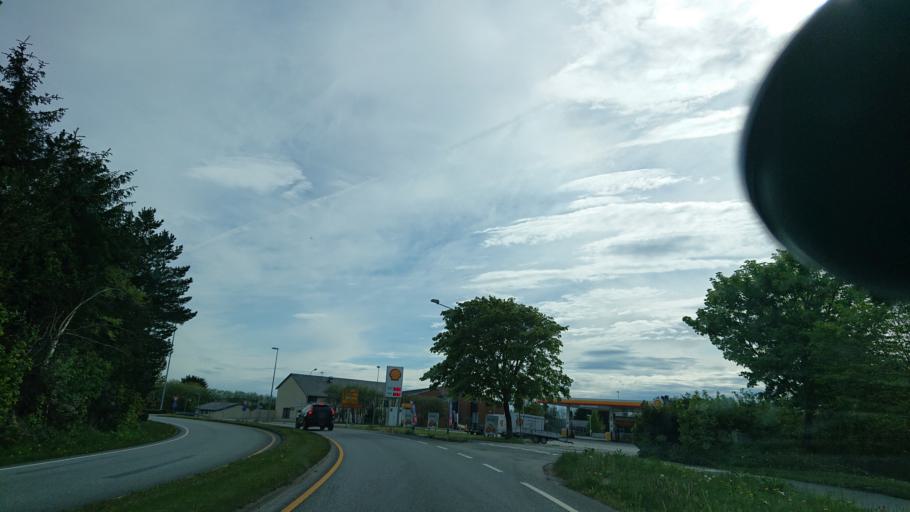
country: NO
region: Rogaland
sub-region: Sola
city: Tananger
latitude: 58.9368
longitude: 5.6051
